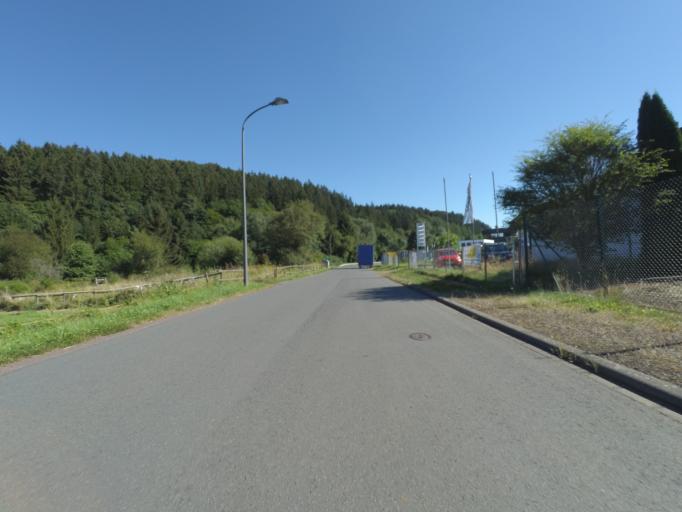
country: DE
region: Rheinland-Pfalz
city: Daun
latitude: 50.2177
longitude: 6.8418
